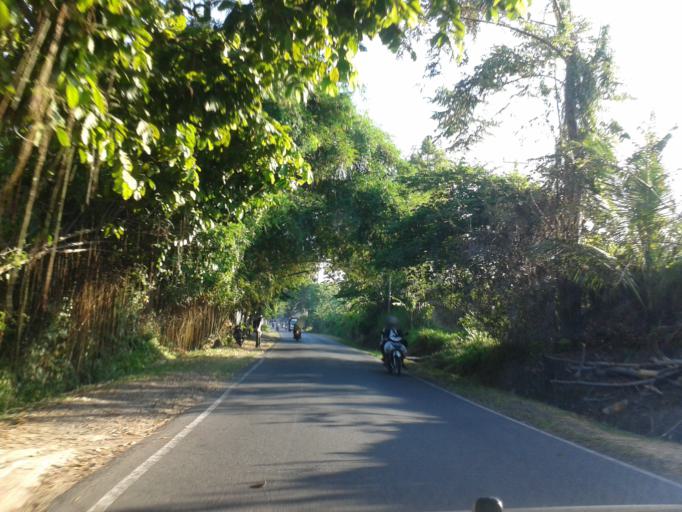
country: ID
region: Bali
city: Klungkung
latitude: -8.5093
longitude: 115.4023
